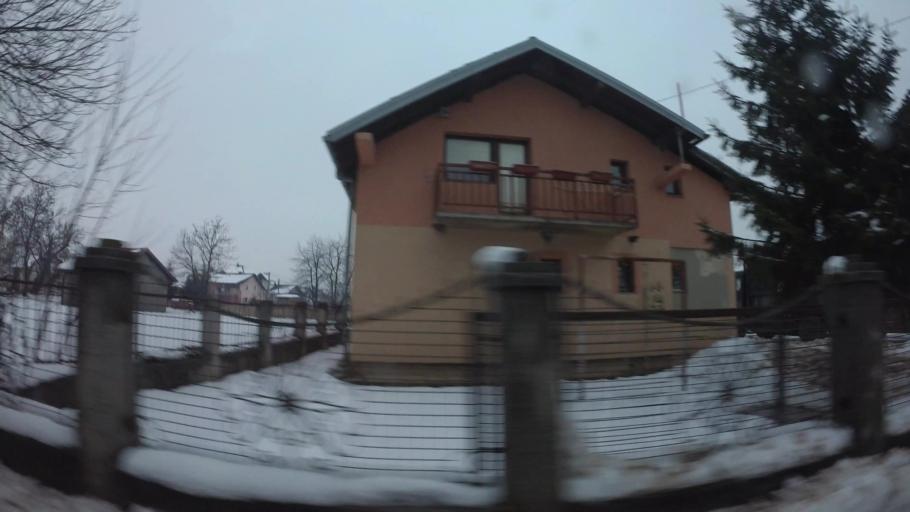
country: BA
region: Federation of Bosnia and Herzegovina
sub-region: Kanton Sarajevo
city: Sarajevo
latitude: 43.8444
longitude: 18.3026
